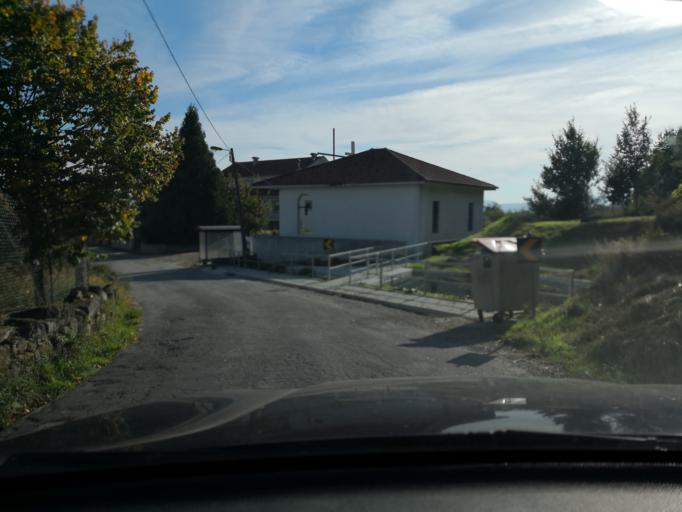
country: PT
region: Vila Real
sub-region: Vila Real
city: Vila Real
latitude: 41.3344
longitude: -7.7432
